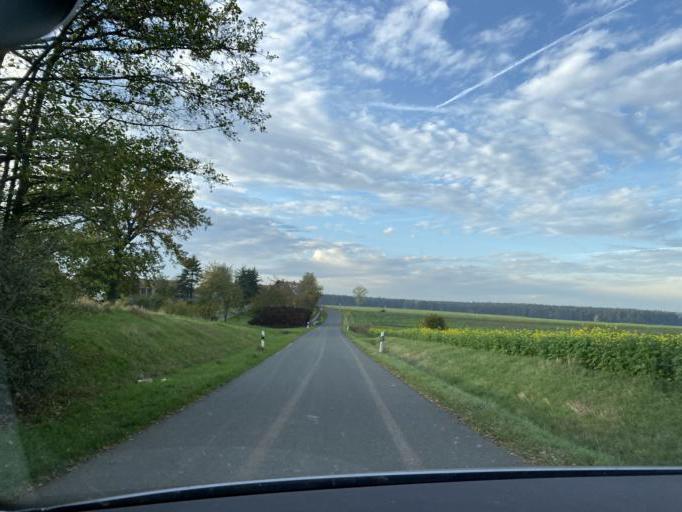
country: DE
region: Bavaria
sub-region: Regierungsbezirk Mittelfranken
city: Puschendorf
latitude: 49.5441
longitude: 10.8347
